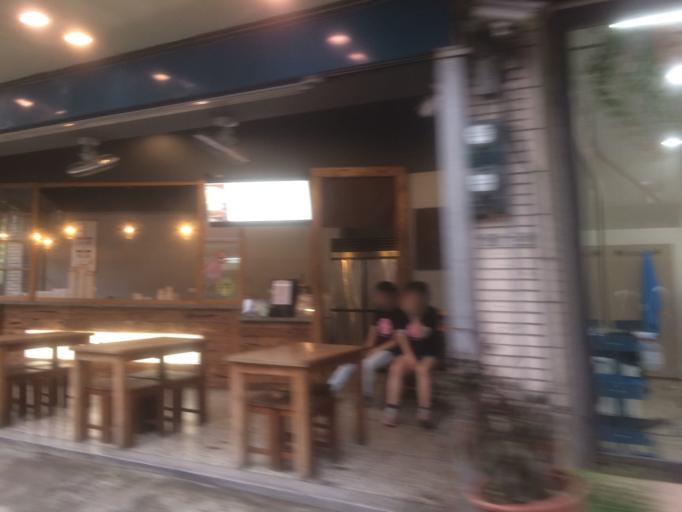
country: TW
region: Taiwan
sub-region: Yilan
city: Yilan
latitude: 24.6746
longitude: 121.7712
